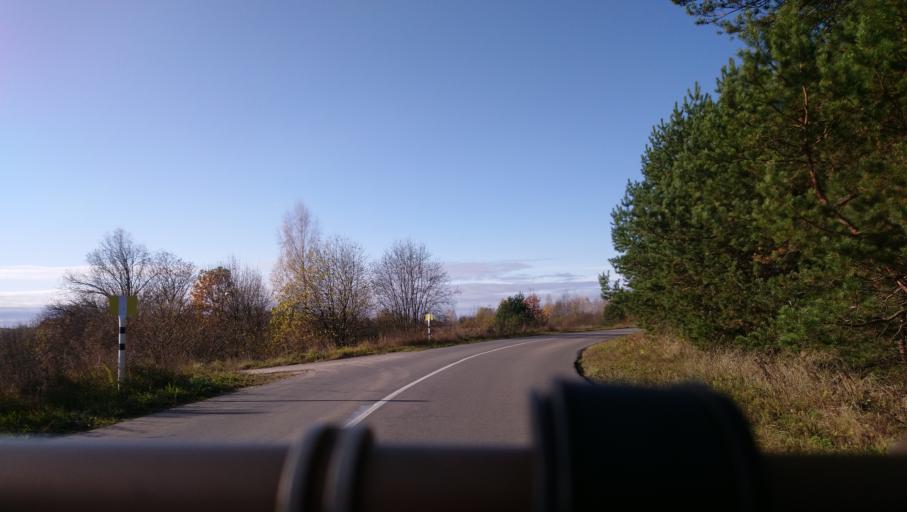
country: RU
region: Moskovskaya
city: Dubna
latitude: 56.7753
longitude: 37.2278
